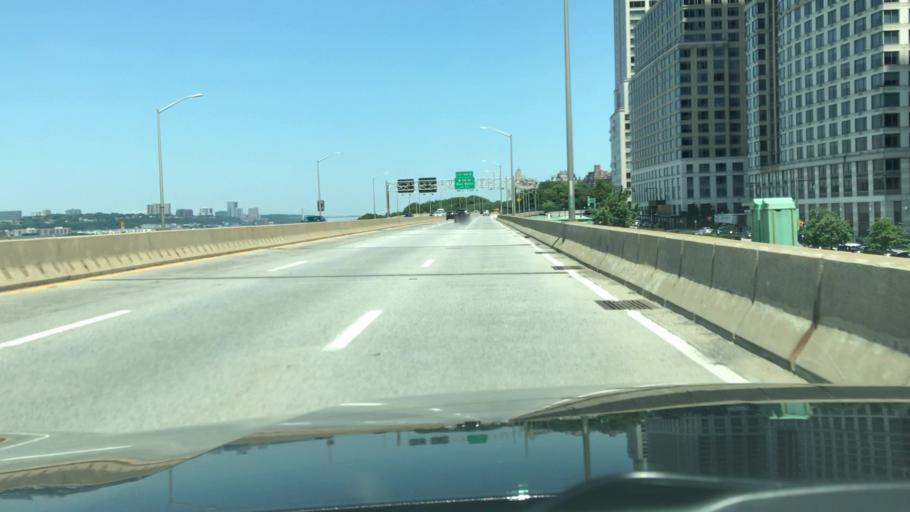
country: US
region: New Jersey
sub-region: Hudson County
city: Guttenberg
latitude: 40.7781
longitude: -73.9895
